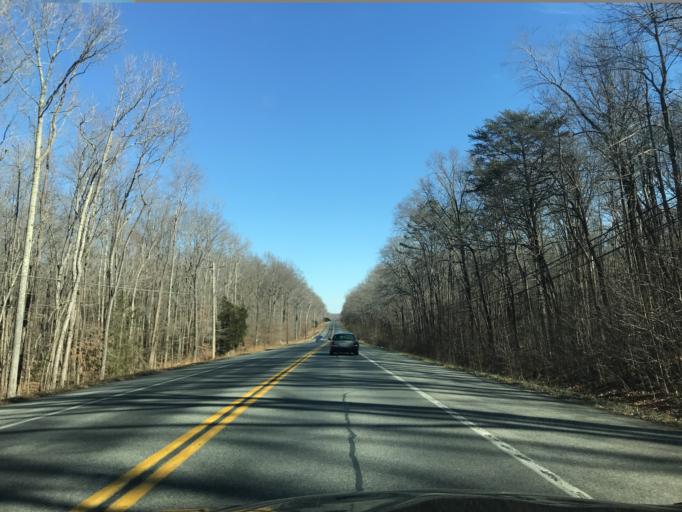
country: US
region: Maryland
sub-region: Charles County
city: Potomac Heights
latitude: 38.5789
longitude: -77.1392
